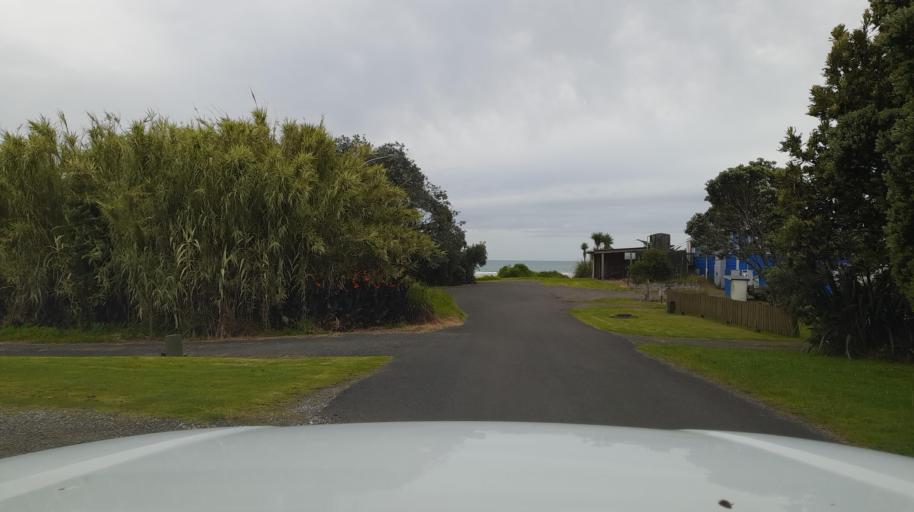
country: NZ
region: Northland
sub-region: Far North District
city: Ahipara
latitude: -35.1672
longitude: 173.1533
